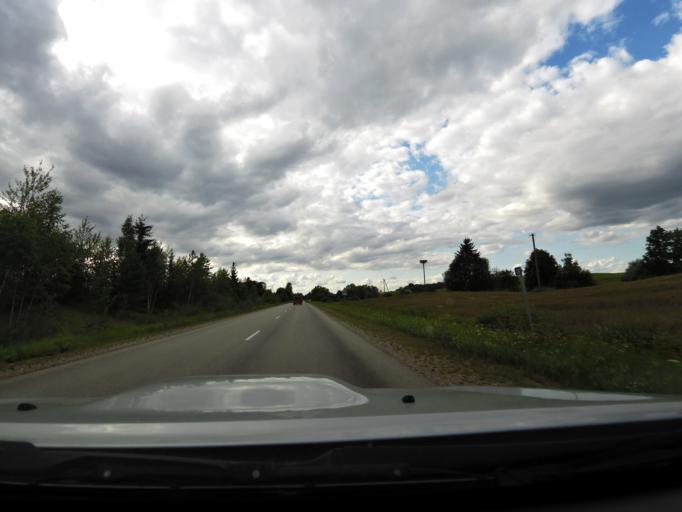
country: LV
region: Ilukste
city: Ilukste
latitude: 55.9762
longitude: 26.0156
